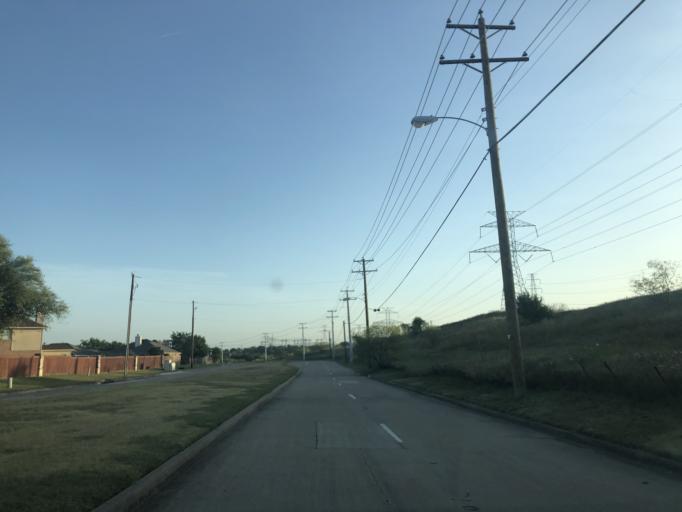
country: US
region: Texas
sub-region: Dallas County
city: Duncanville
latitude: 32.6553
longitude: -96.9611
